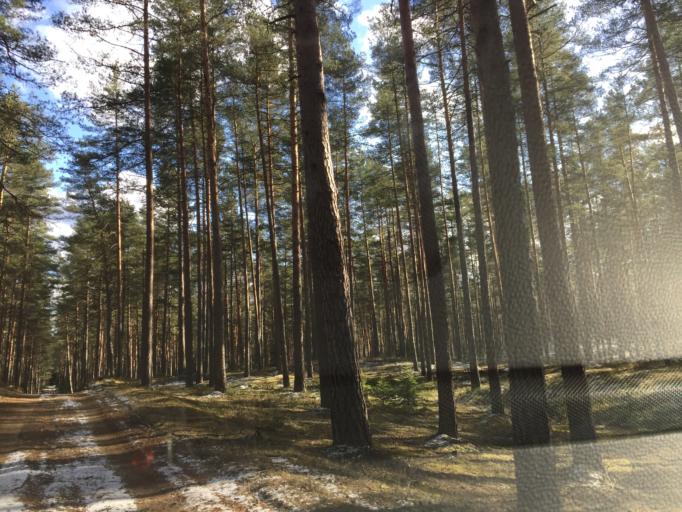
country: LV
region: Garkalne
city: Garkalne
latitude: 56.9636
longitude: 24.4522
